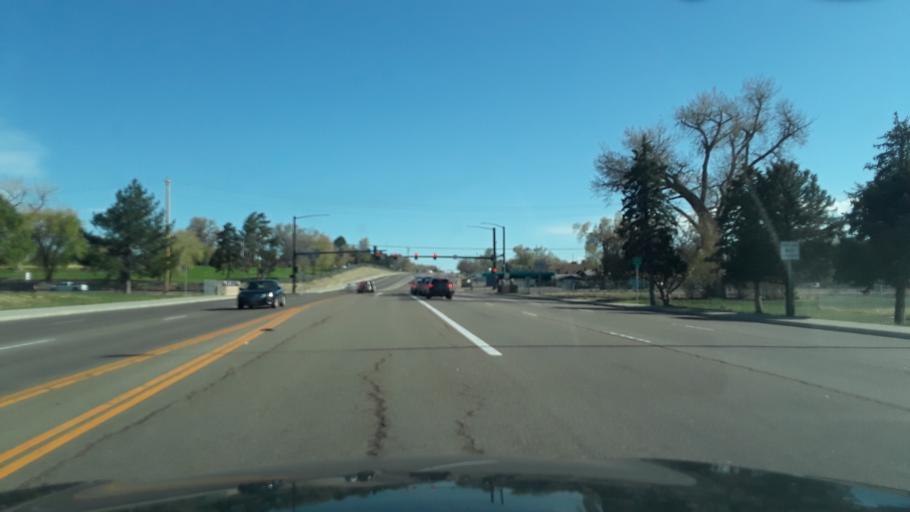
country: US
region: Colorado
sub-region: Pueblo County
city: Pueblo
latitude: 38.2595
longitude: -104.6616
